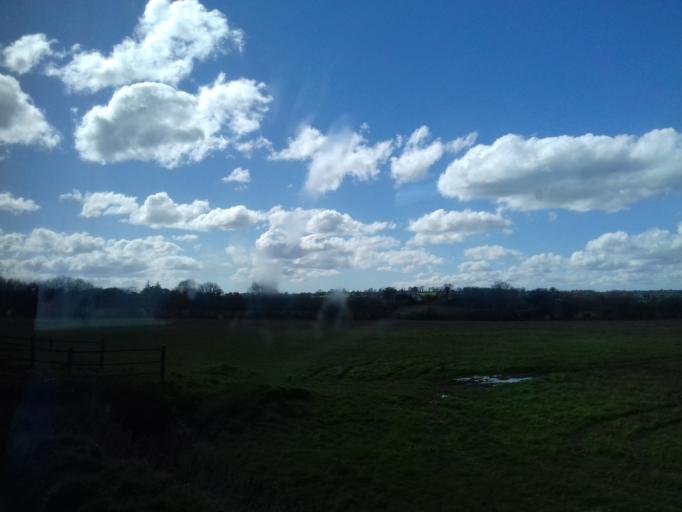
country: IE
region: Munster
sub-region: County Cork
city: Kanturk
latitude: 52.1212
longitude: -8.9209
